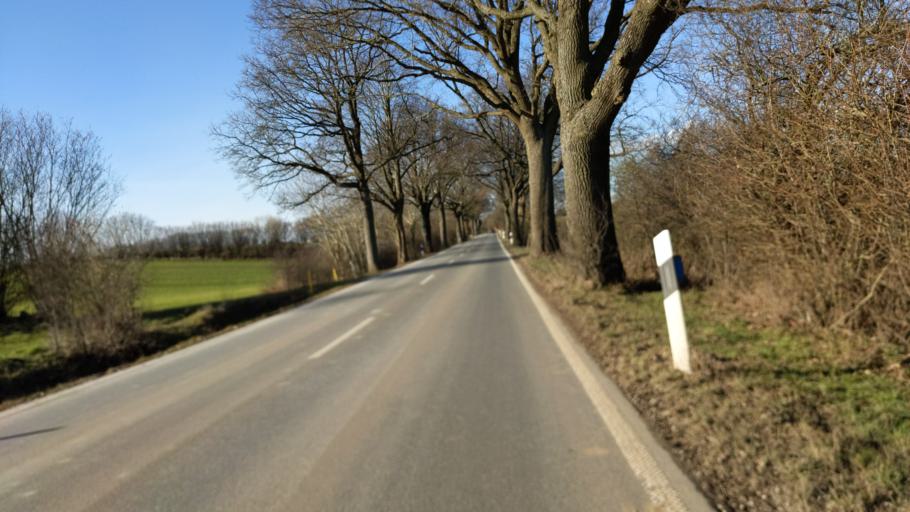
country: DE
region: Schleswig-Holstein
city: Susel
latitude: 54.0586
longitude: 10.6505
